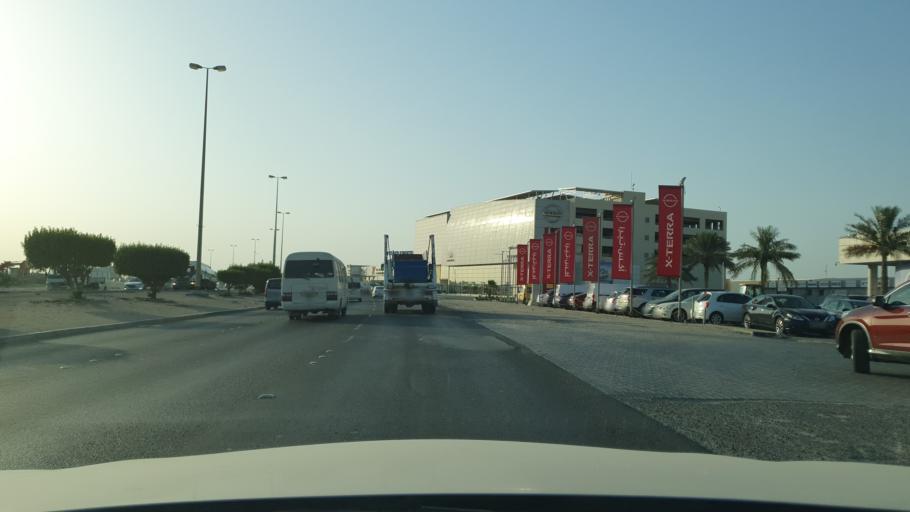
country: BH
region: Northern
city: Sitrah
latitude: 26.1505
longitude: 50.6178
